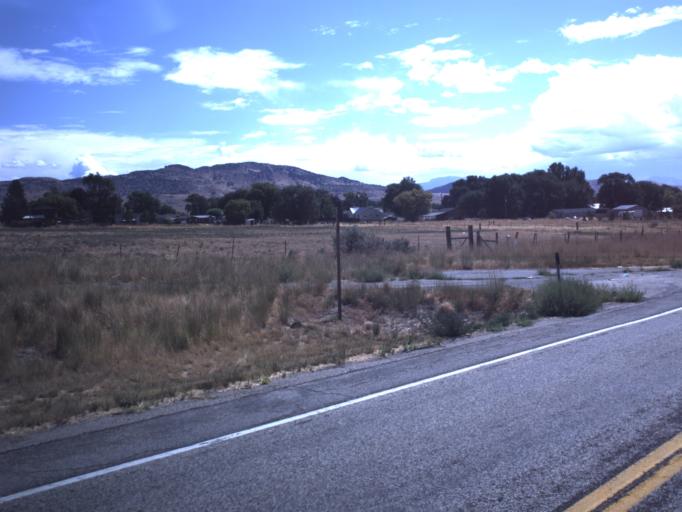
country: US
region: Utah
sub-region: Box Elder County
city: Garland
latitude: 41.8765
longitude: -112.1516
